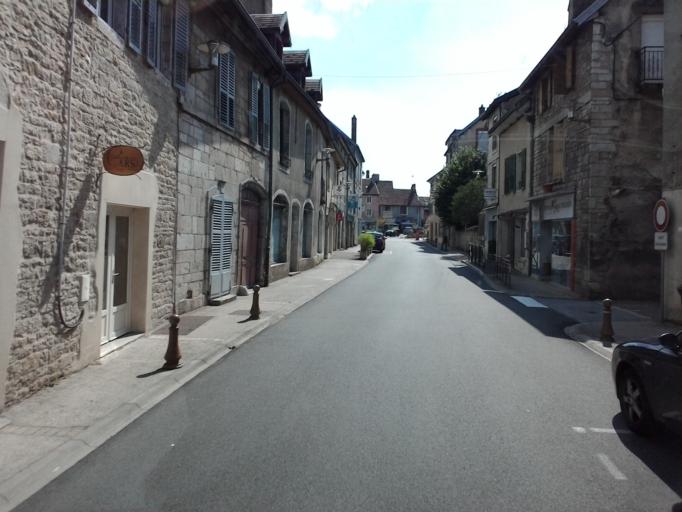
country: FR
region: Franche-Comte
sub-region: Departement du Doubs
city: Quingey
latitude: 47.1038
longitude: 5.8845
